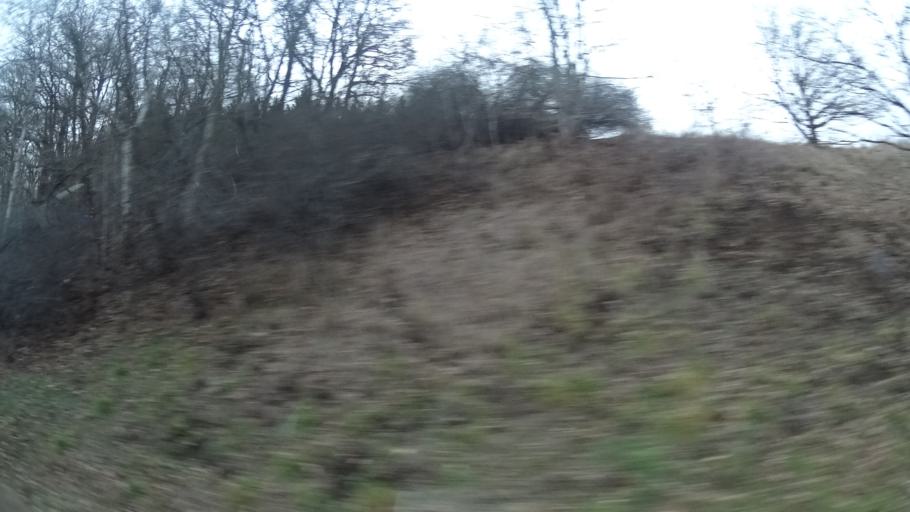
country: DE
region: Thuringia
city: Zeulenroda
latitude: 50.6658
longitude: 11.9646
